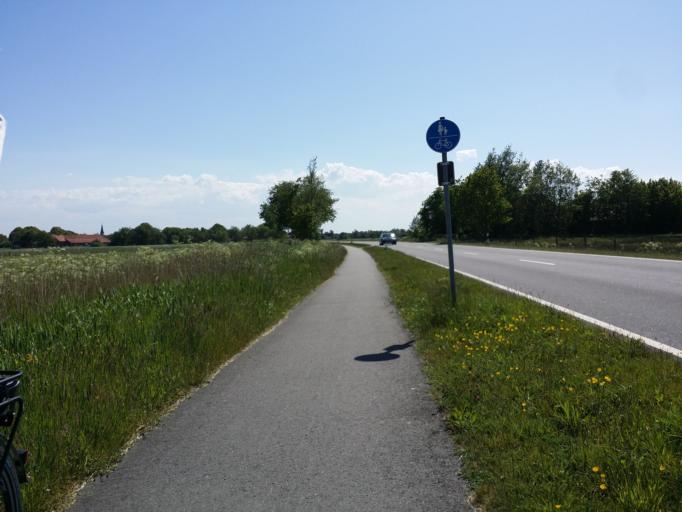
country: DE
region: Lower Saxony
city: Esens
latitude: 53.6620
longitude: 7.6130
